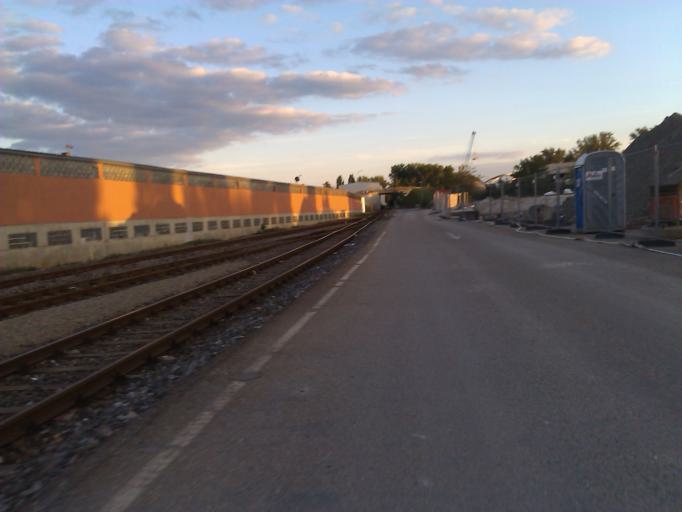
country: DE
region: Baden-Wuerttemberg
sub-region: Regierungsbezirk Stuttgart
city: Neckarsulm
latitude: 49.1676
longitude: 9.2079
